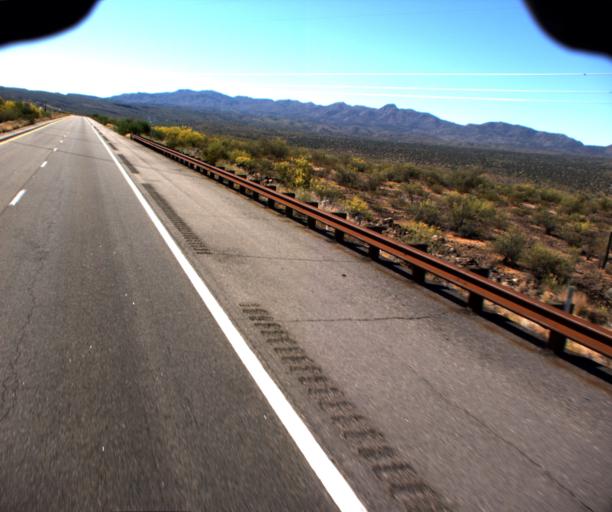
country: US
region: Arizona
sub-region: Yavapai County
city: Bagdad
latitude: 34.5299
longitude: -113.4302
